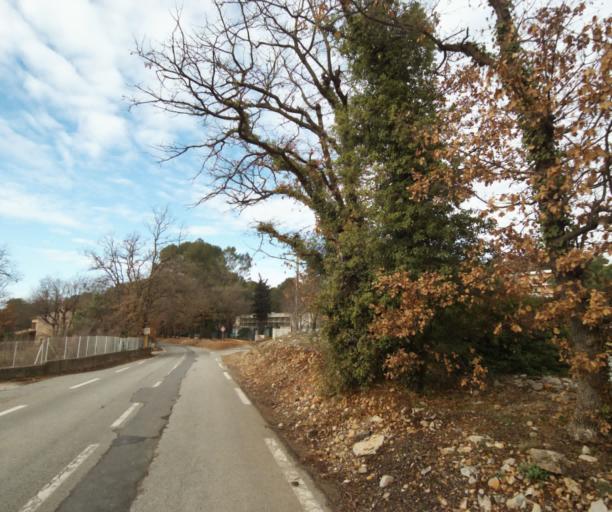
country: FR
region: Provence-Alpes-Cote d'Azur
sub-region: Departement du Var
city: Trans-en-Provence
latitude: 43.5228
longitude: 6.4998
